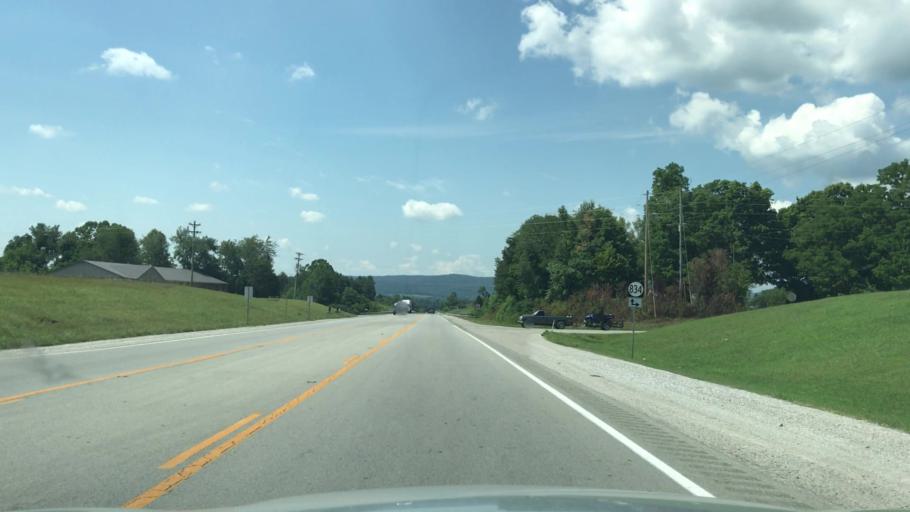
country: US
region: Kentucky
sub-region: Wayne County
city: Monticello
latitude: 36.7772
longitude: -84.9558
